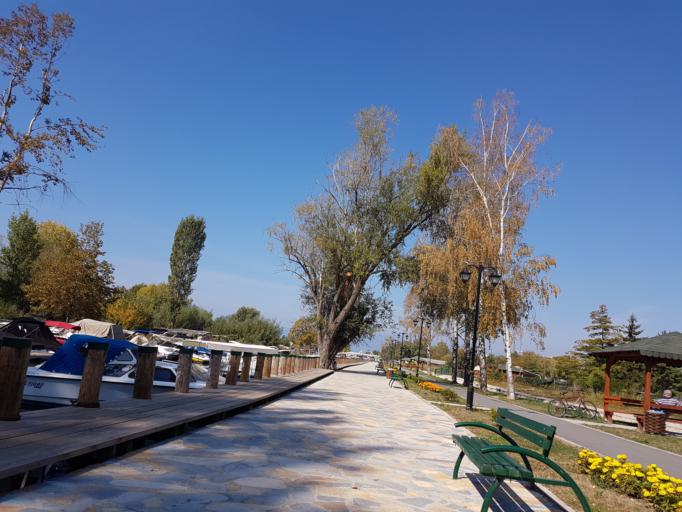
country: MK
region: Ohrid
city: Ohrid
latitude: 41.1029
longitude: 20.8122
